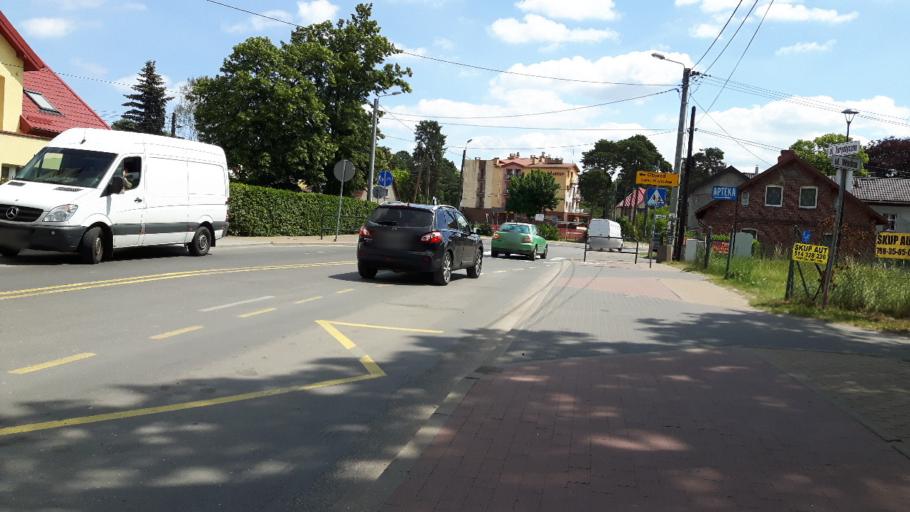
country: PL
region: Pomeranian Voivodeship
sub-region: Powiat gdanski
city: Cedry Wielkie
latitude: 54.3440
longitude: 18.8292
